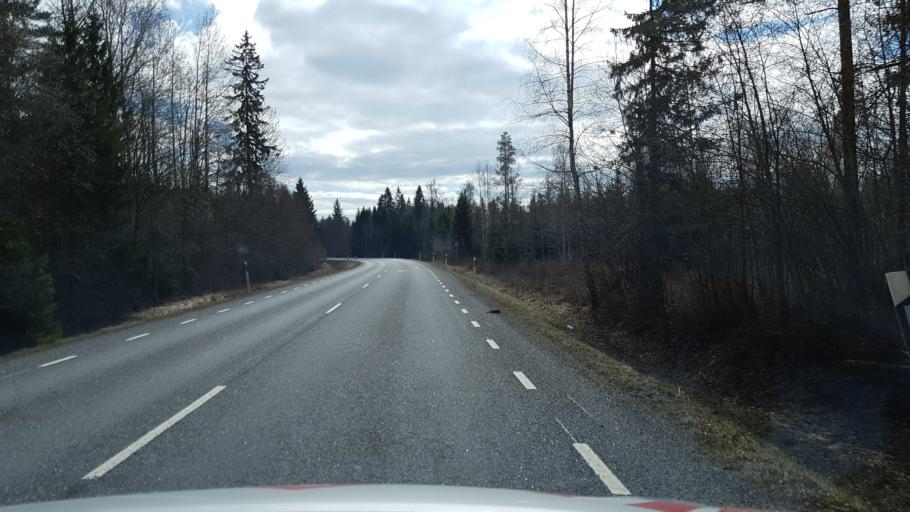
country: EE
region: Laeaene-Virumaa
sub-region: Vaeike-Maarja vald
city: Vaike-Maarja
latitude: 59.0940
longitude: 26.2296
